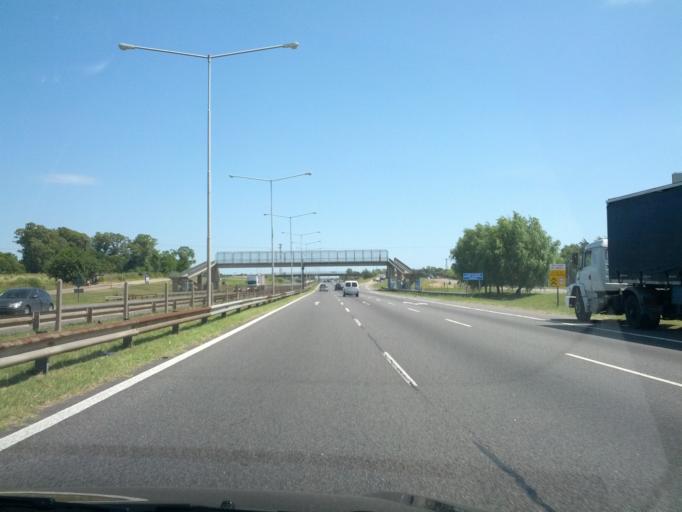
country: AR
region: Buenos Aires
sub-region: Partido de Campana
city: Campana
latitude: -34.2313
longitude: -58.9147
